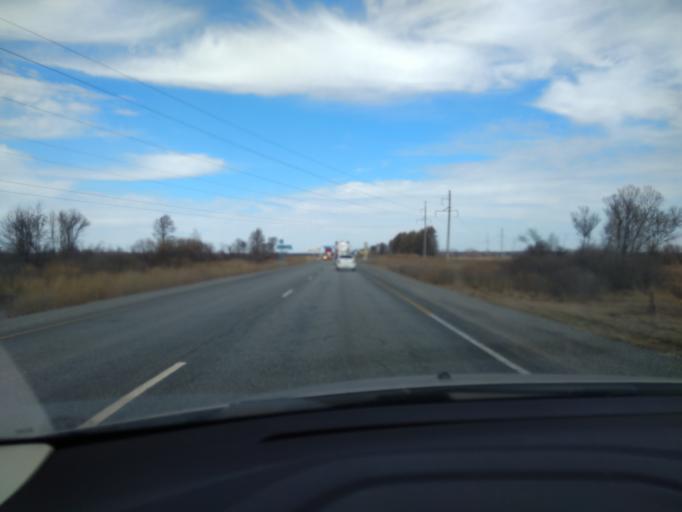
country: RU
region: Sverdlovsk
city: Pyshma
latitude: 57.0271
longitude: 63.4061
